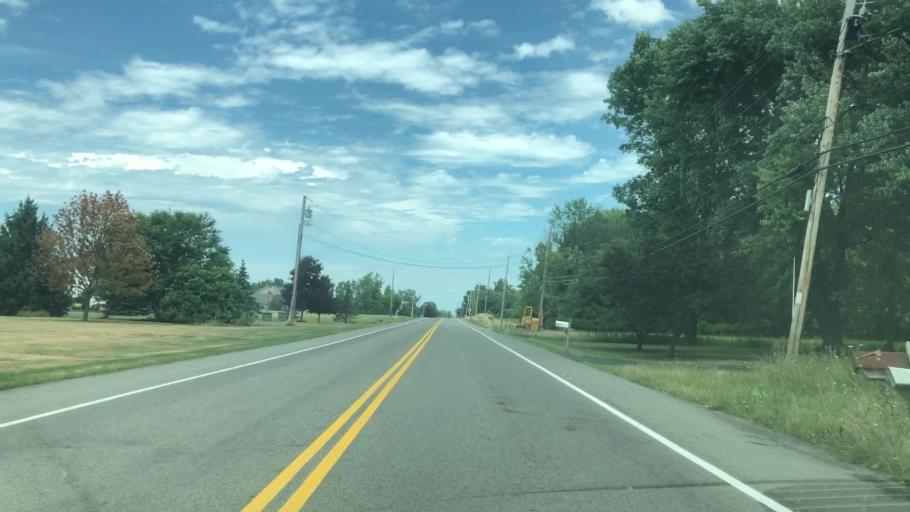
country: US
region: New York
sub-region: Monroe County
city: Webster
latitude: 43.1983
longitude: -77.4004
